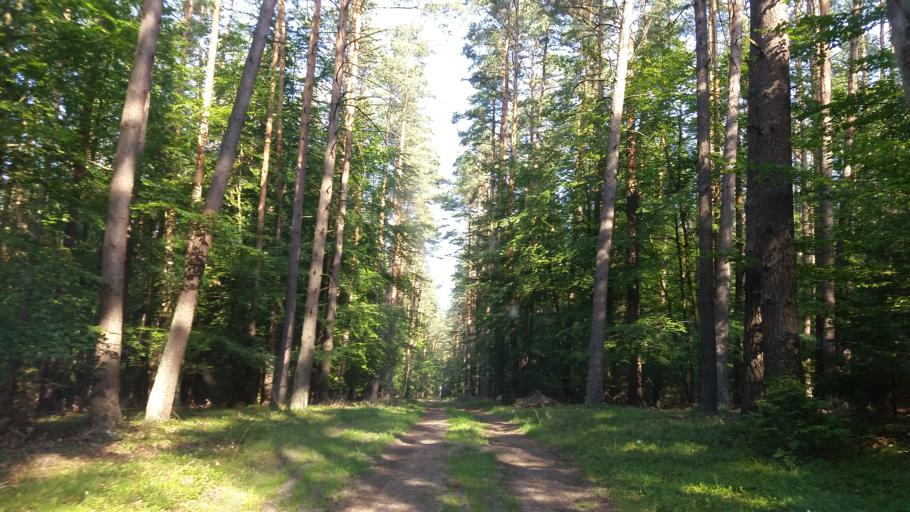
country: PL
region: West Pomeranian Voivodeship
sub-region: Powiat choszczenski
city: Pelczyce
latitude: 52.9662
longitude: 15.3605
